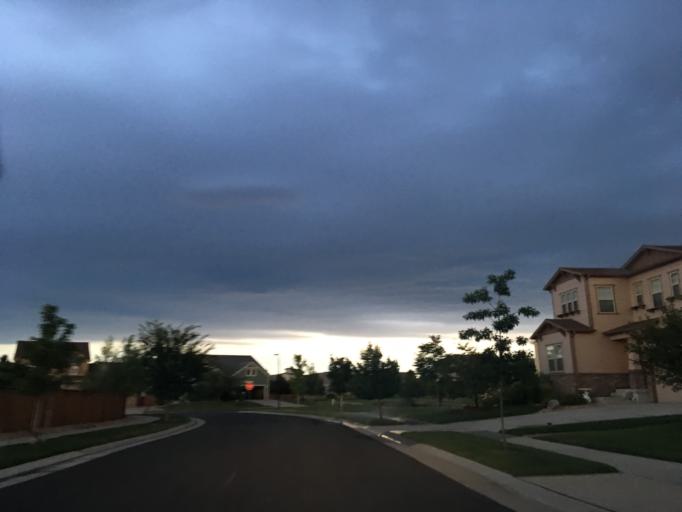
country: US
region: Colorado
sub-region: Douglas County
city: Stonegate
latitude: 39.5094
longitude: -104.8095
